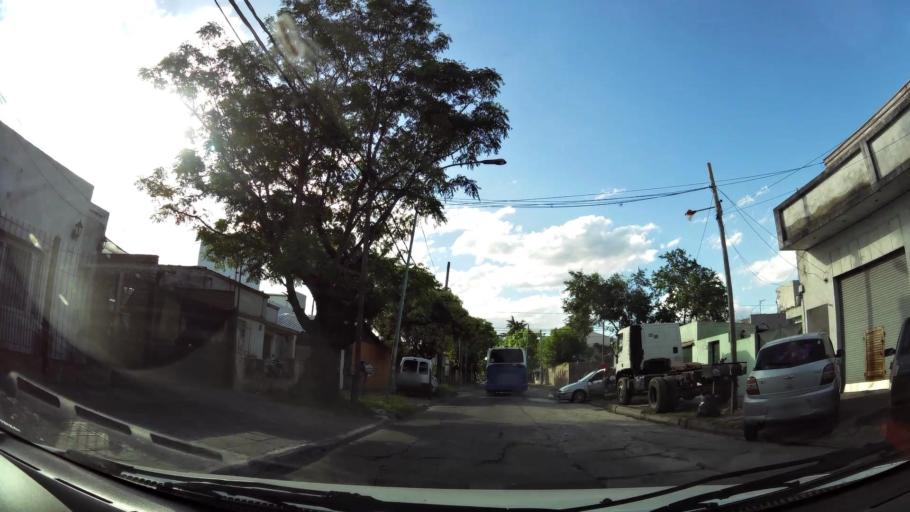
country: AR
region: Buenos Aires
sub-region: Partido de General San Martin
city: General San Martin
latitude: -34.5382
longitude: -58.5503
